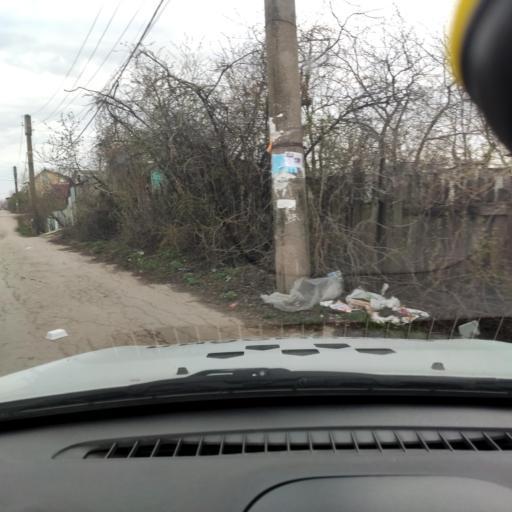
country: RU
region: Samara
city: Mezhdurechensk
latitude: 53.2452
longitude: 49.1474
